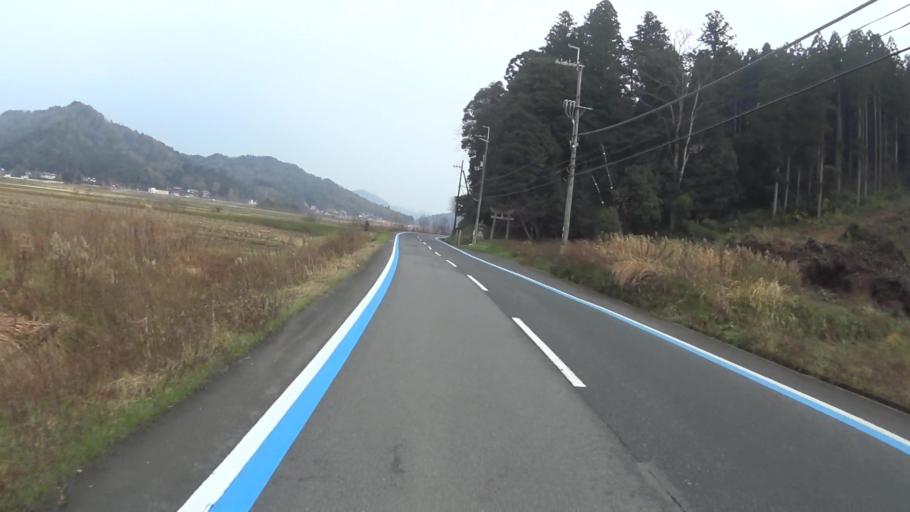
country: JP
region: Kyoto
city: Ayabe
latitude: 35.4048
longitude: 135.1882
